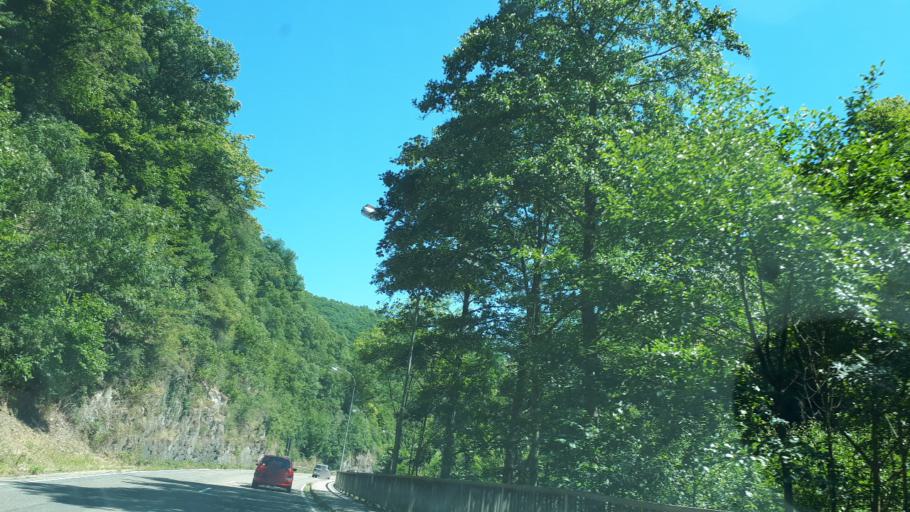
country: DE
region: Rheinland-Pfalz
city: Cochem
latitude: 50.1575
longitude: 7.1462
